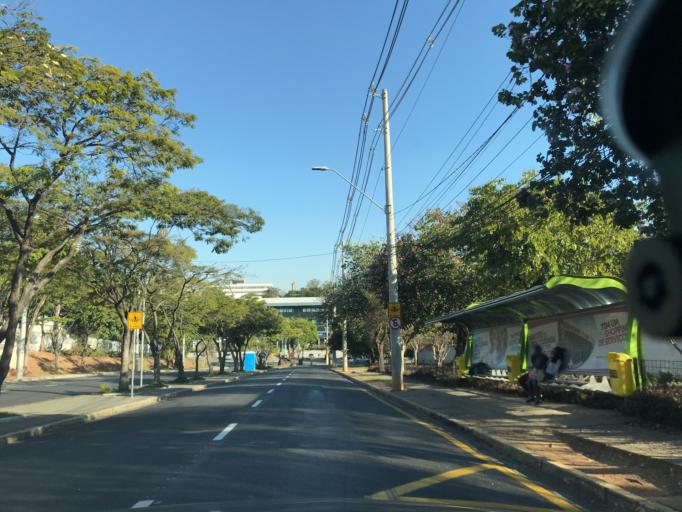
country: BR
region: Sao Paulo
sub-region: Barueri
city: Barueri
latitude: -23.4965
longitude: -46.8538
